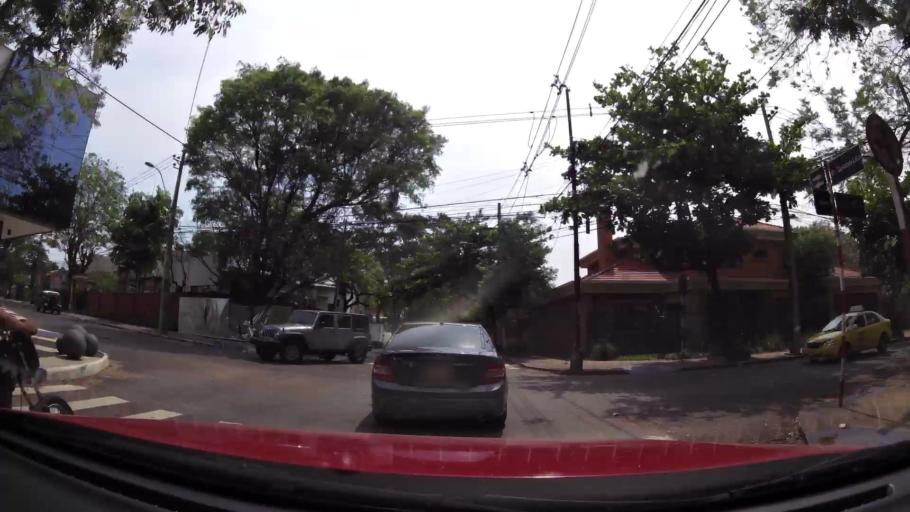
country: PY
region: Asuncion
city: Asuncion
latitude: -25.2873
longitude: -57.5812
